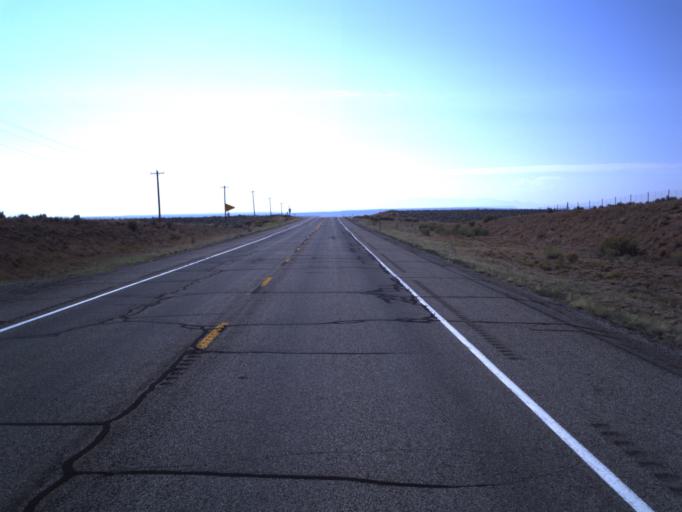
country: US
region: Utah
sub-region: San Juan County
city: Blanding
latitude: 37.5011
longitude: -109.4859
